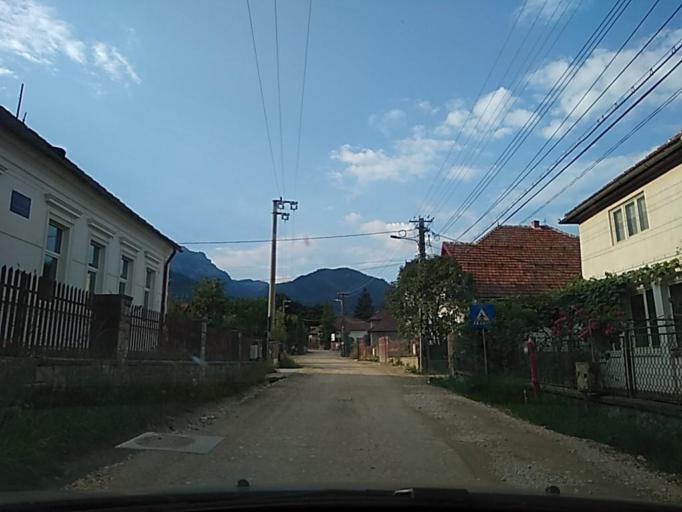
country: RO
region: Brasov
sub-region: Comuna Bran
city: Sohodol
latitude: 45.5034
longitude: 25.3827
